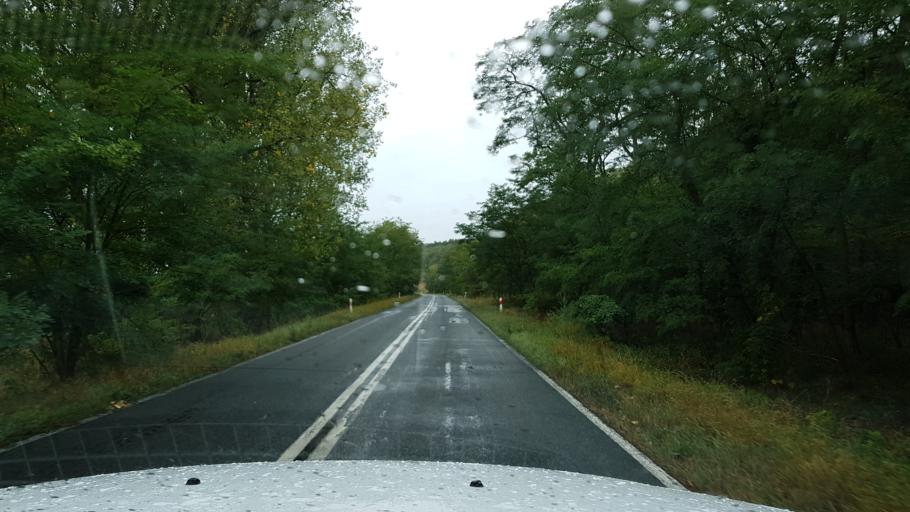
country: PL
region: West Pomeranian Voivodeship
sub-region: Powiat gryfinski
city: Cedynia
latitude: 52.8324
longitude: 14.1684
